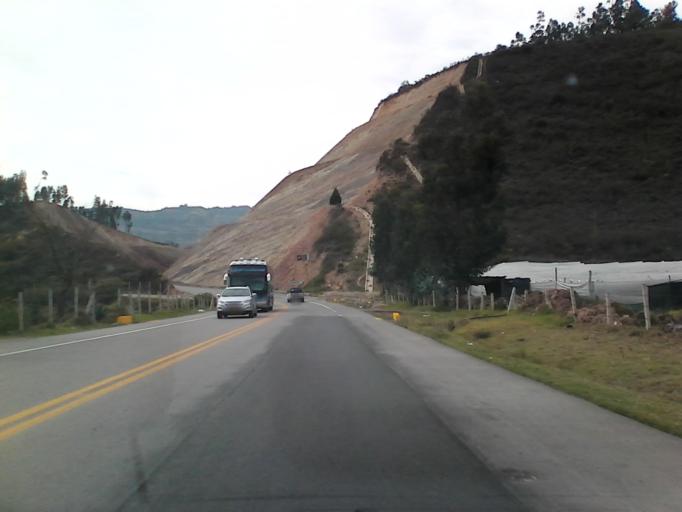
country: CO
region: Boyaca
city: Tibasosa
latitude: 5.7596
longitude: -72.9957
